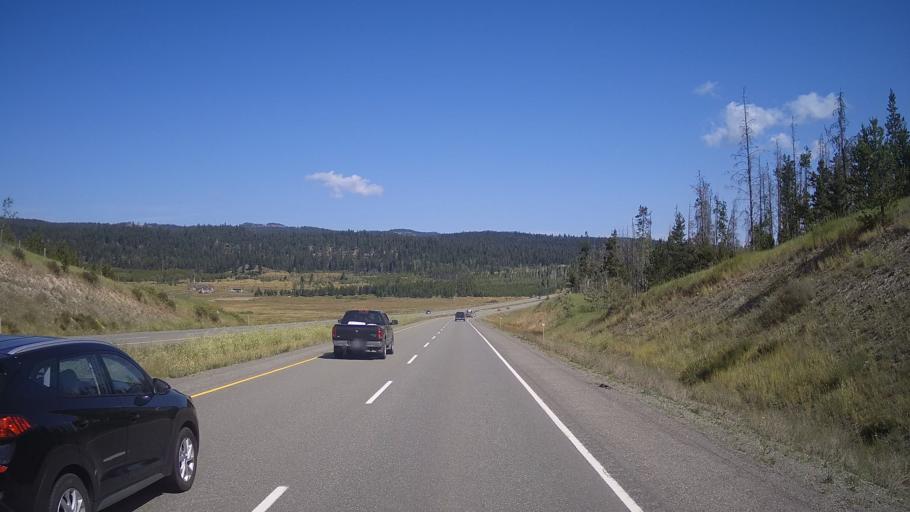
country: CA
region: British Columbia
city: Logan Lake
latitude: 50.4549
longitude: -120.5915
